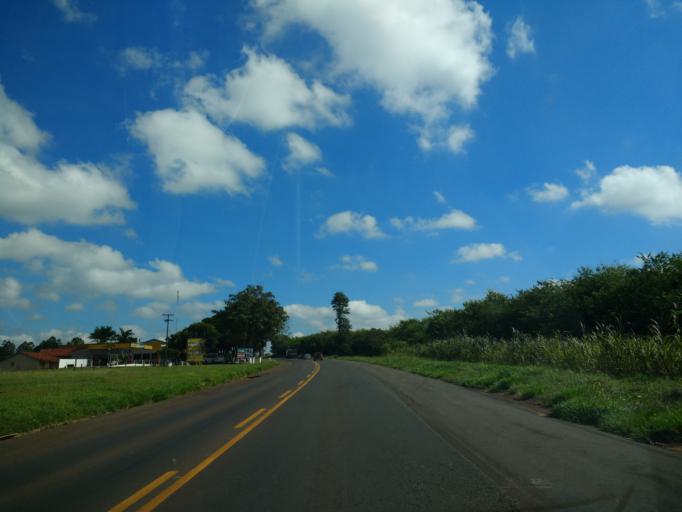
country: BR
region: Parana
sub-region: Umuarama
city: Umuarama
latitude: -23.8298
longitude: -53.3514
